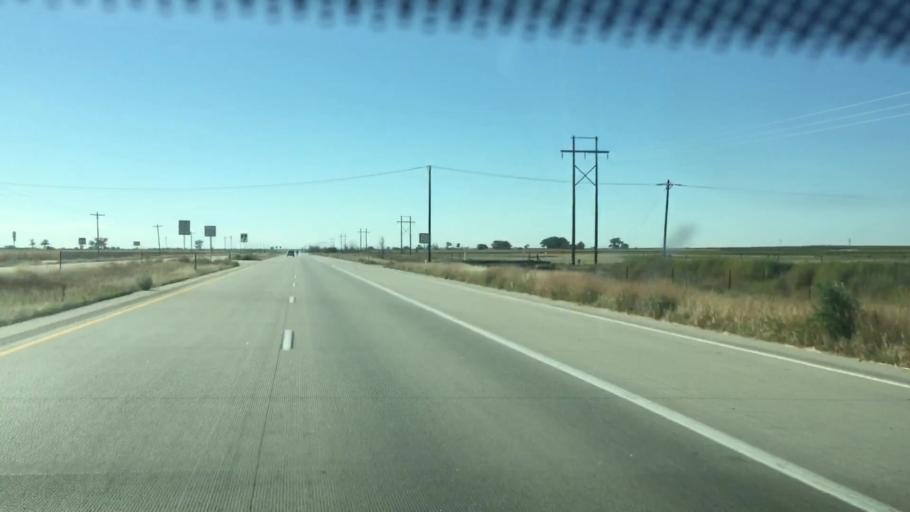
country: US
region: Colorado
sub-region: Prowers County
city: Lamar
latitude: 38.1109
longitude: -102.6674
